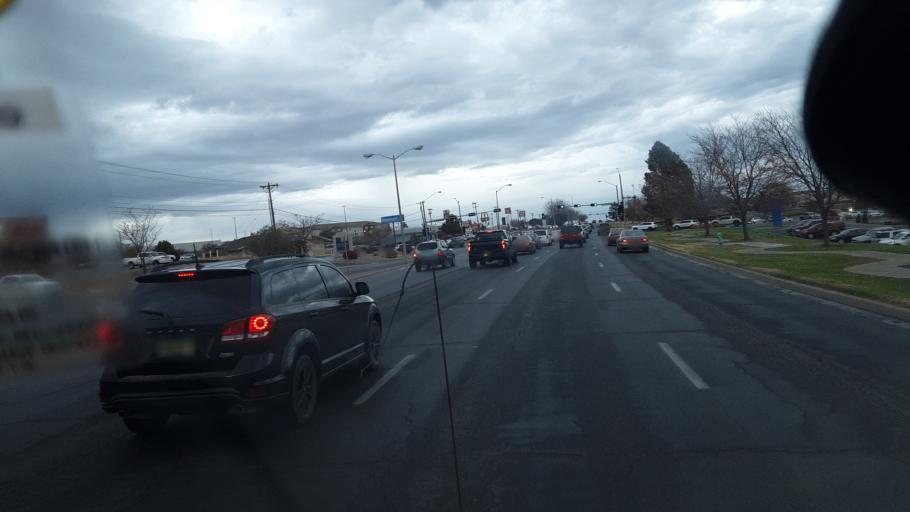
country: US
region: New Mexico
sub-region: San Juan County
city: Farmington
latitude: 36.7645
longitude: -108.1529
